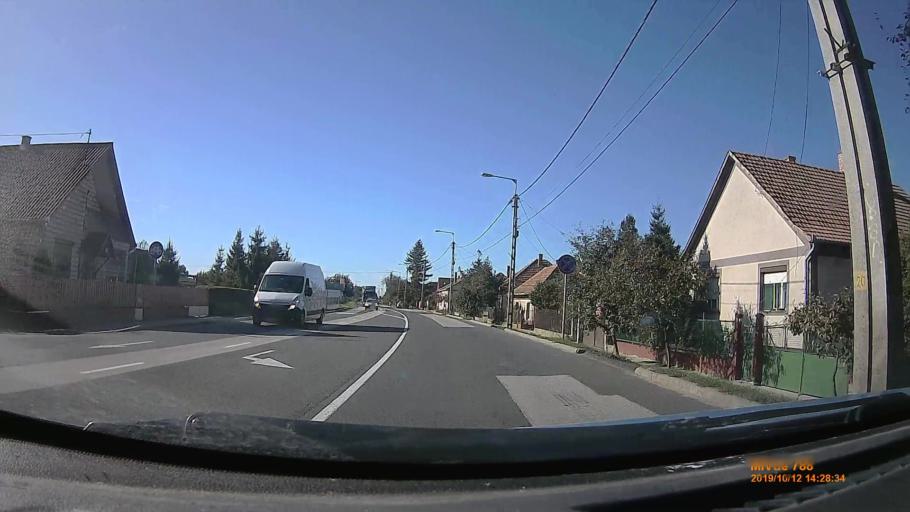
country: HU
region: Hajdu-Bihar
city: Berettyoujfalu
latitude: 47.1678
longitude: 21.6228
